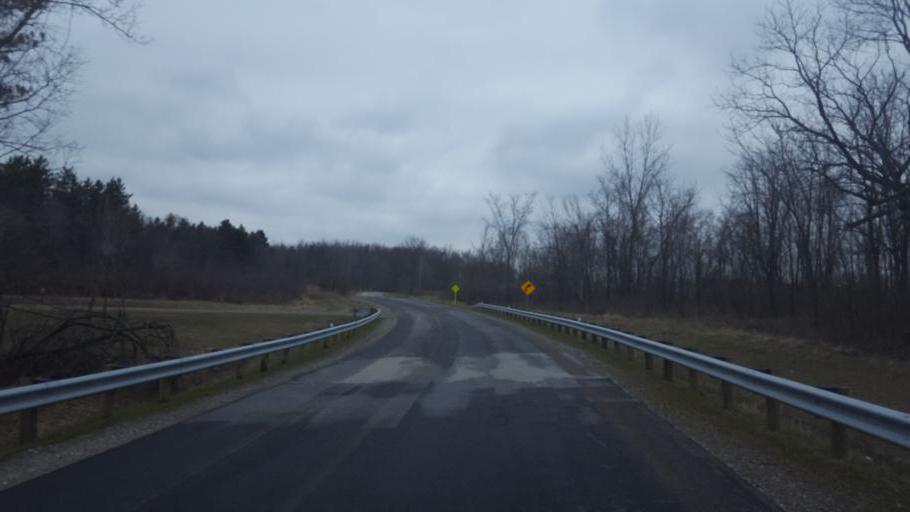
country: US
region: Ohio
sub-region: Delaware County
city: Ashley
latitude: 40.4247
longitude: -83.0098
